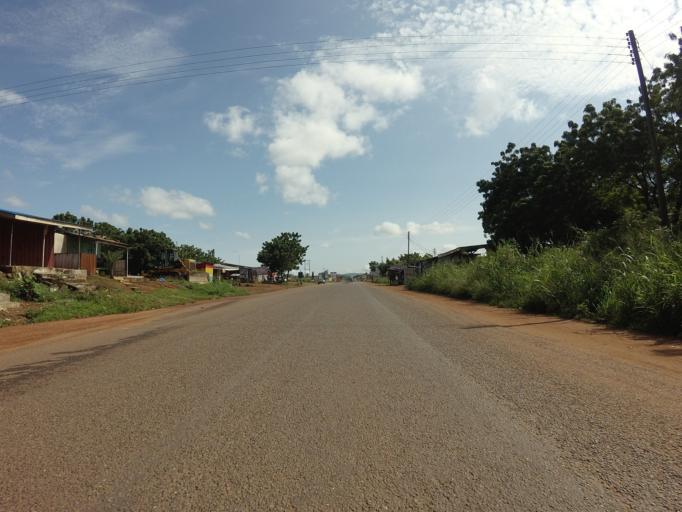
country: GH
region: Eastern
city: Aburi
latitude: 5.8065
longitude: -0.1247
